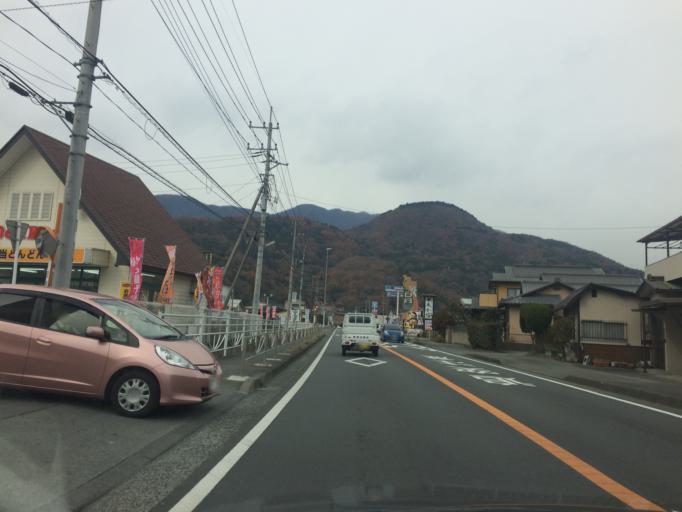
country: JP
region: Yamanashi
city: Ryuo
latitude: 35.4331
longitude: 138.4422
